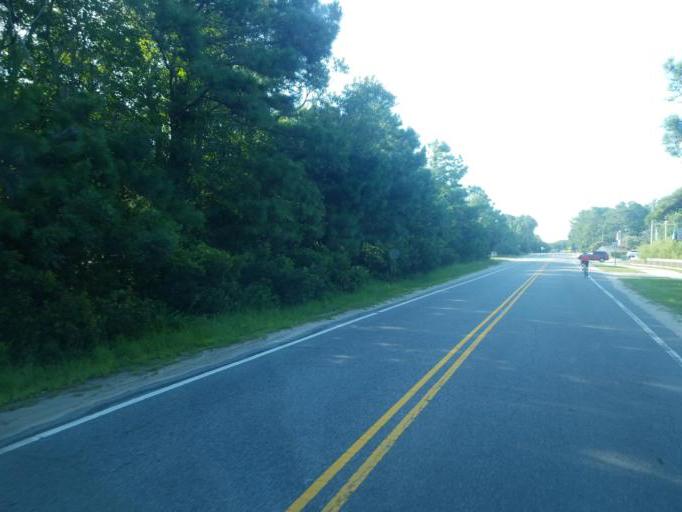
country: US
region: North Carolina
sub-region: Currituck County
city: Currituck
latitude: 36.3811
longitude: -75.8312
